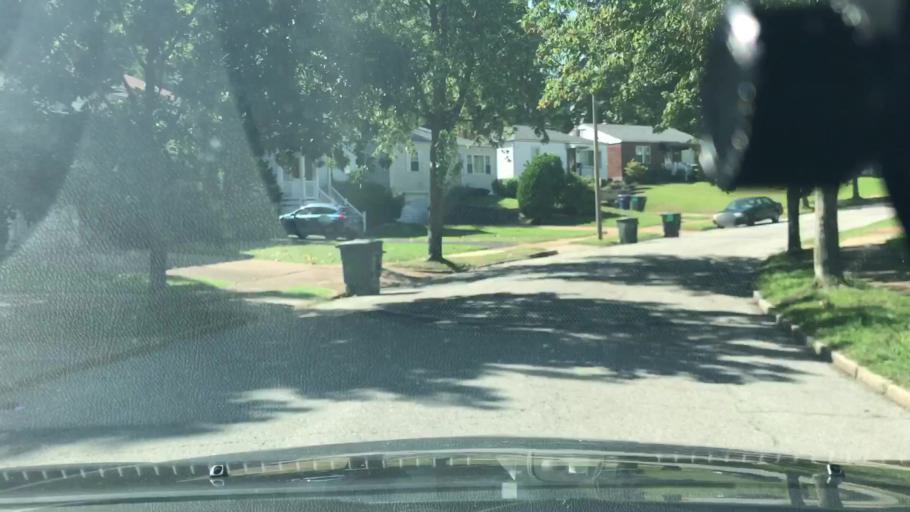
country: US
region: Missouri
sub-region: Saint Louis County
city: Richmond Heights
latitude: 38.6148
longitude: -90.2895
